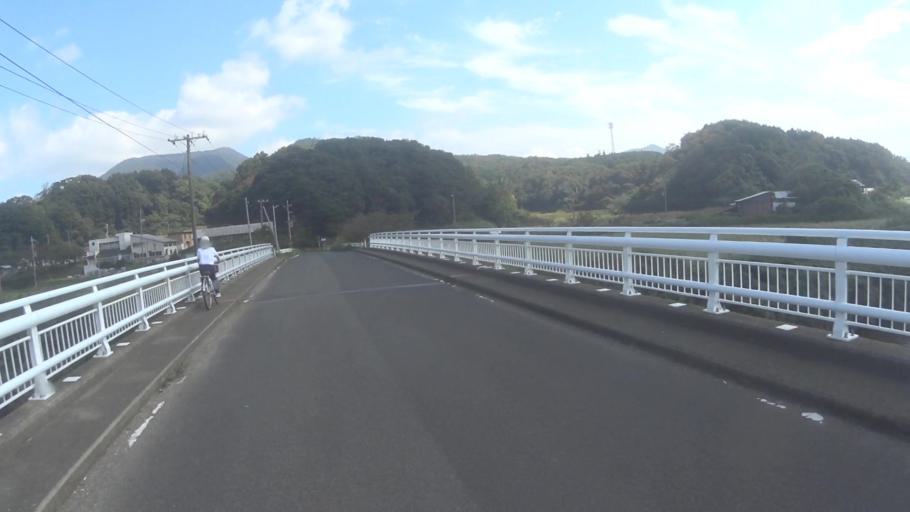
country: JP
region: Kyoto
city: Miyazu
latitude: 35.7291
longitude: 135.1018
